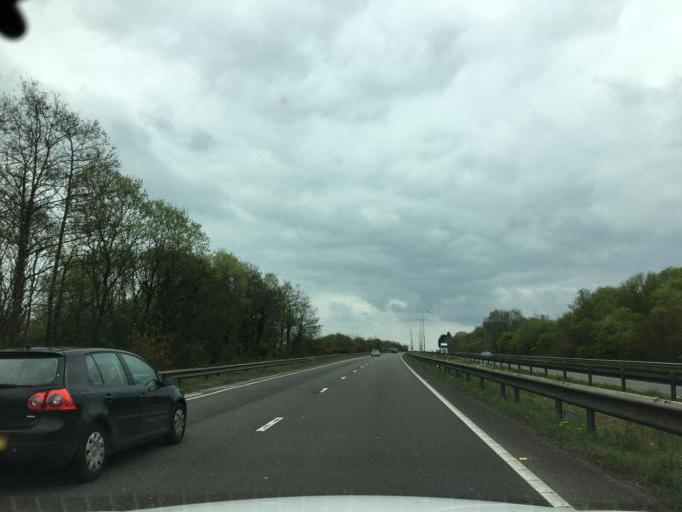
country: GB
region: Wales
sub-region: Carmarthenshire
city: Cross Hands
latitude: 51.7822
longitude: -4.0737
